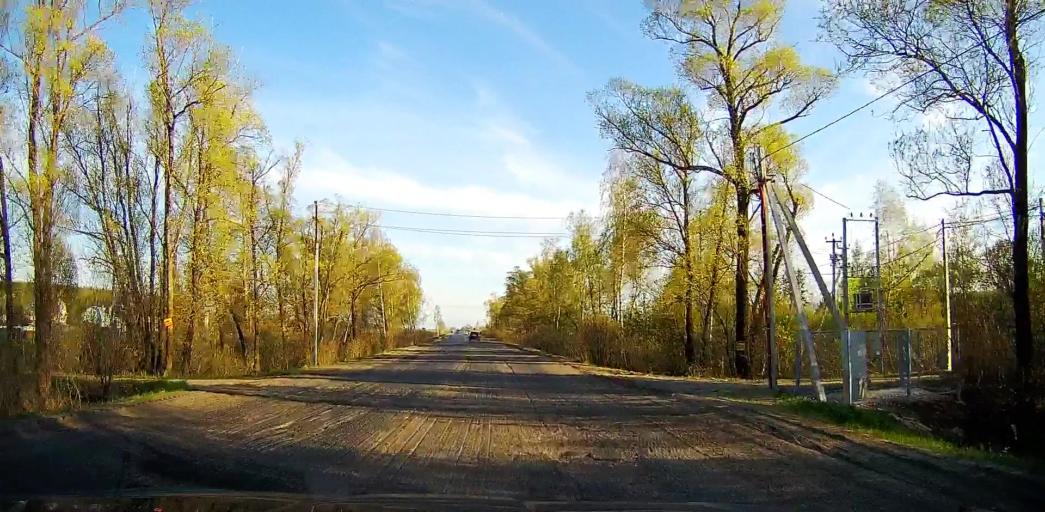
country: RU
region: Moskovskaya
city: Bronnitsy
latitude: 55.3012
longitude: 38.2101
